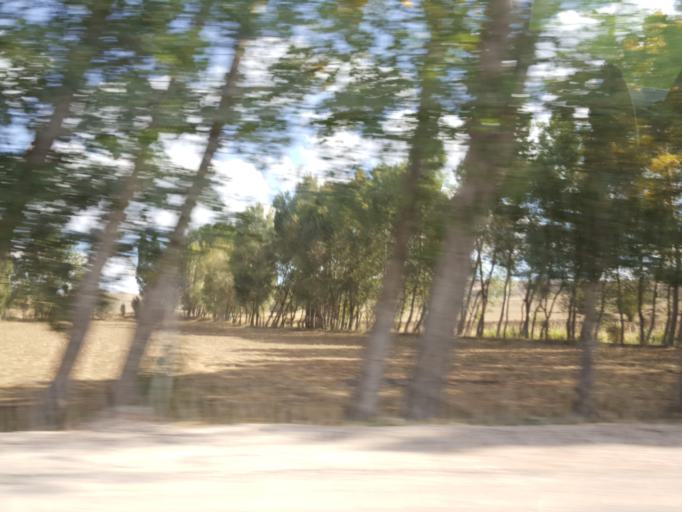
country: TR
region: Tokat
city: Artova
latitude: 40.1443
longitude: 36.3743
